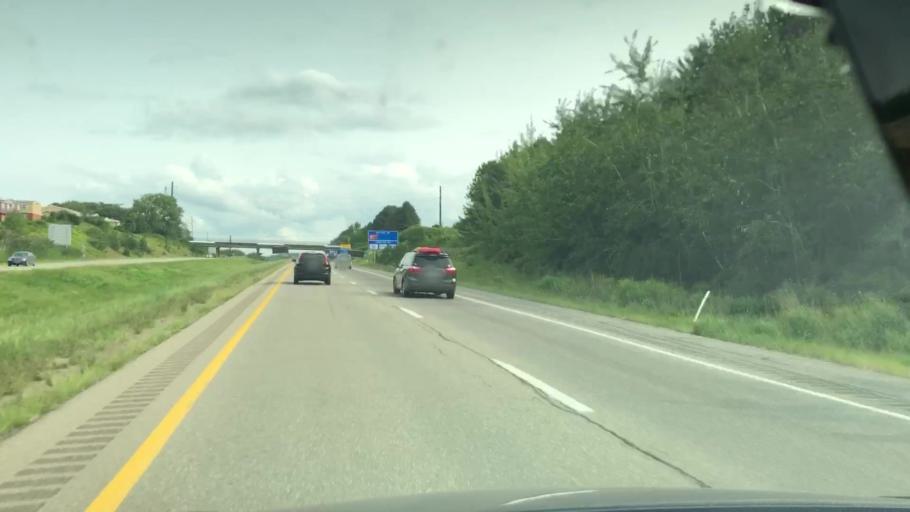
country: US
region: Pennsylvania
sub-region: Erie County
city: Erie
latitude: 42.0809
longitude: -80.1132
